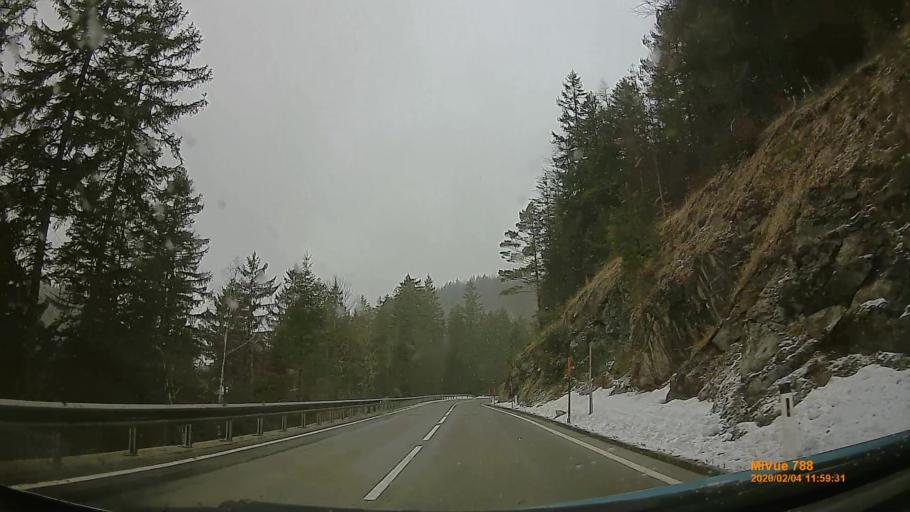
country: AT
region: Styria
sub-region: Politischer Bezirk Bruck-Muerzzuschlag
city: Muerzsteg
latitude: 47.7742
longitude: 15.4948
